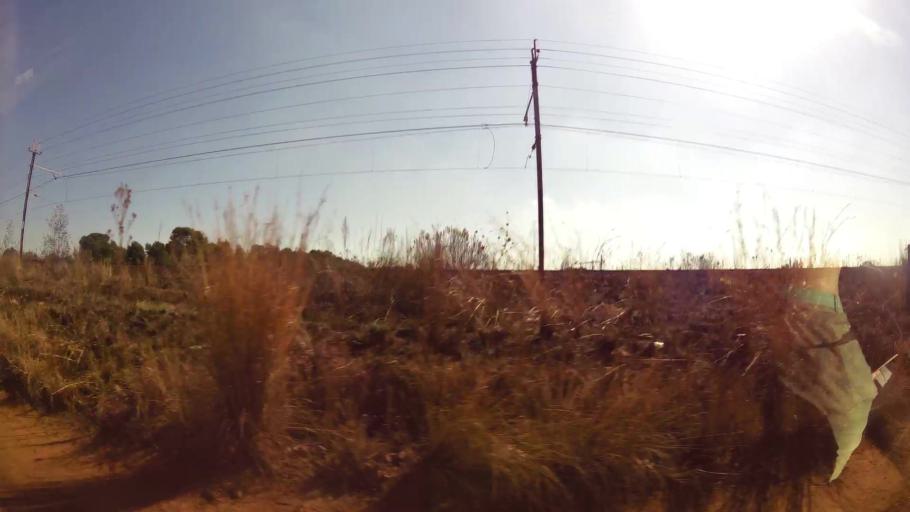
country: ZA
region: Mpumalanga
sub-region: Nkangala District Municipality
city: Witbank
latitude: -25.8268
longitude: 29.2539
